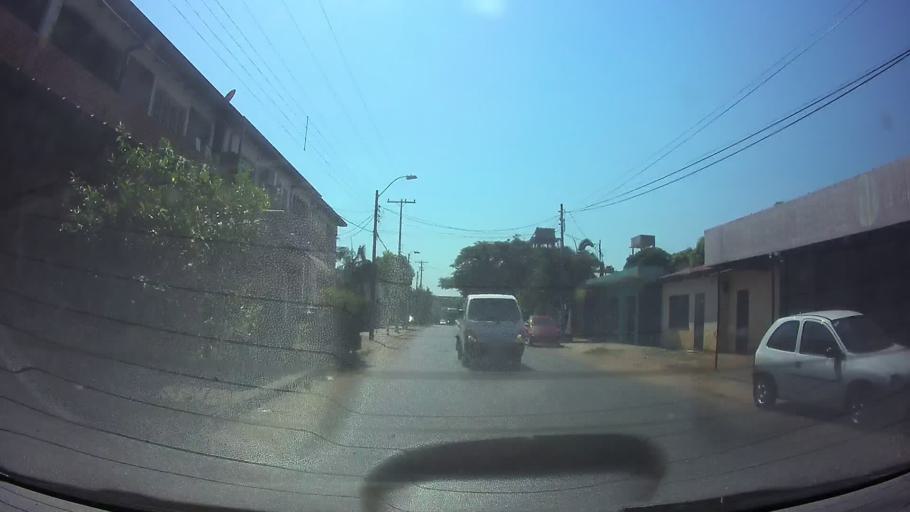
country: PY
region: Central
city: San Lorenzo
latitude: -25.2712
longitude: -57.4992
